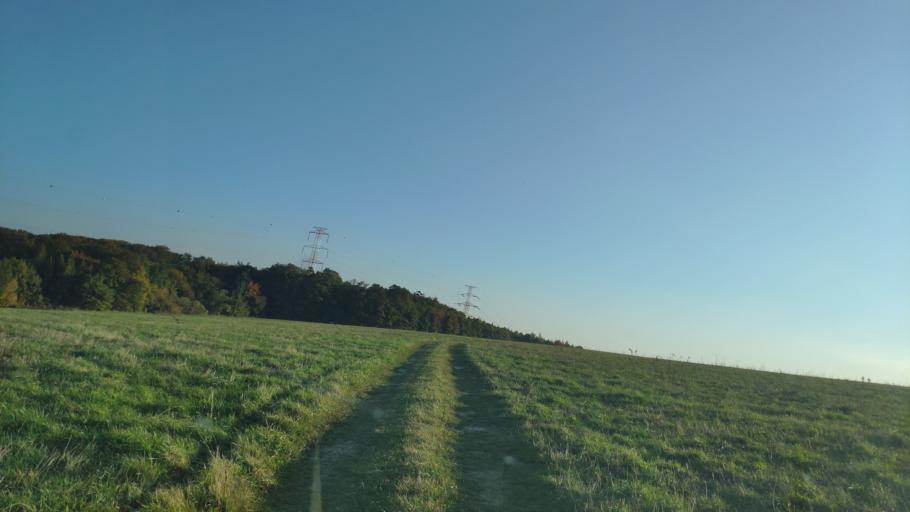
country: SK
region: Kosicky
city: Kosice
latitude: 48.7121
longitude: 21.1688
